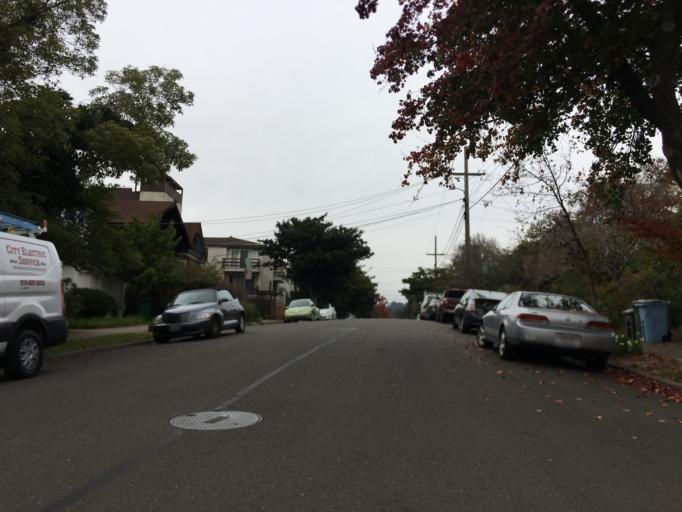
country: US
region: California
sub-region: Alameda County
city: Berkeley
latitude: 37.8825
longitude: -122.2731
